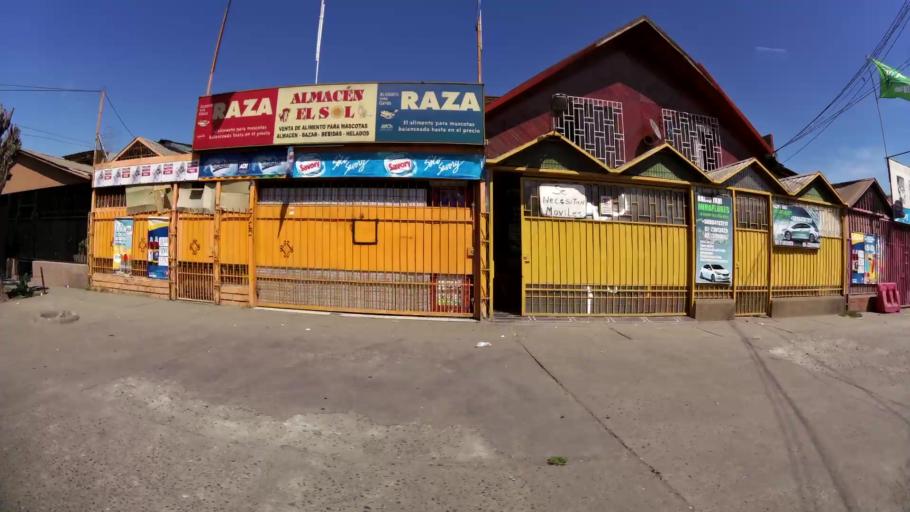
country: CL
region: Santiago Metropolitan
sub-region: Provincia de Santiago
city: Lo Prado
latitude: -33.4066
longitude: -70.7177
